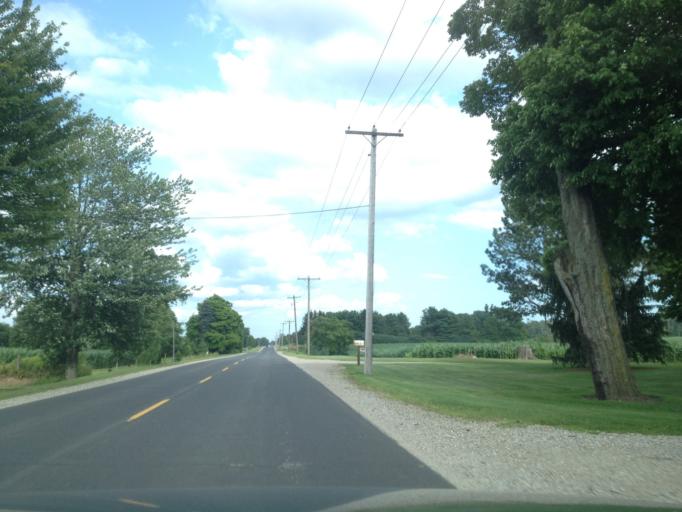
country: CA
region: Ontario
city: Aylmer
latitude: 42.6757
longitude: -80.9715
